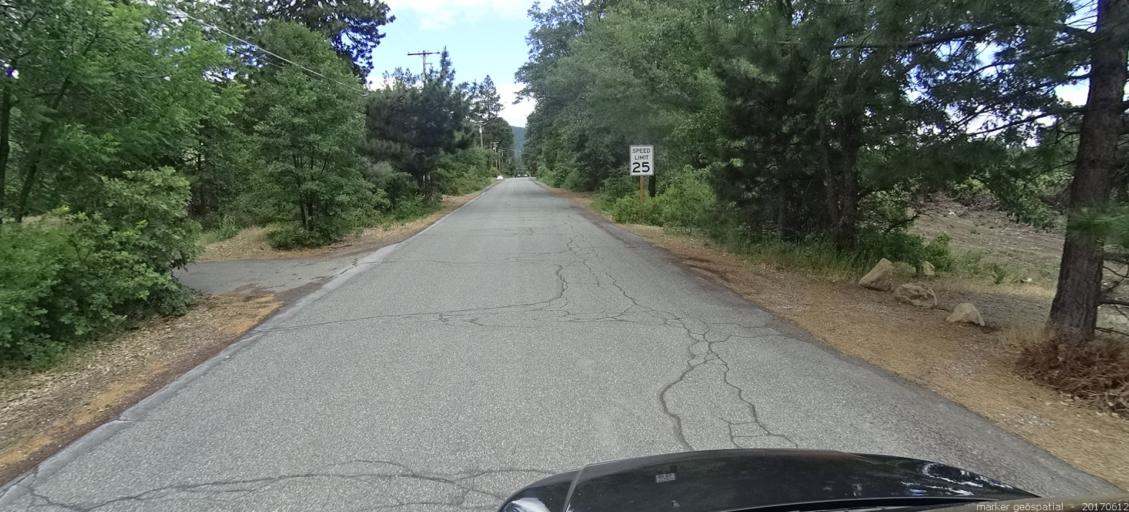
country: US
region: California
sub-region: Siskiyou County
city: Mount Shasta
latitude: 41.3235
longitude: -122.3155
